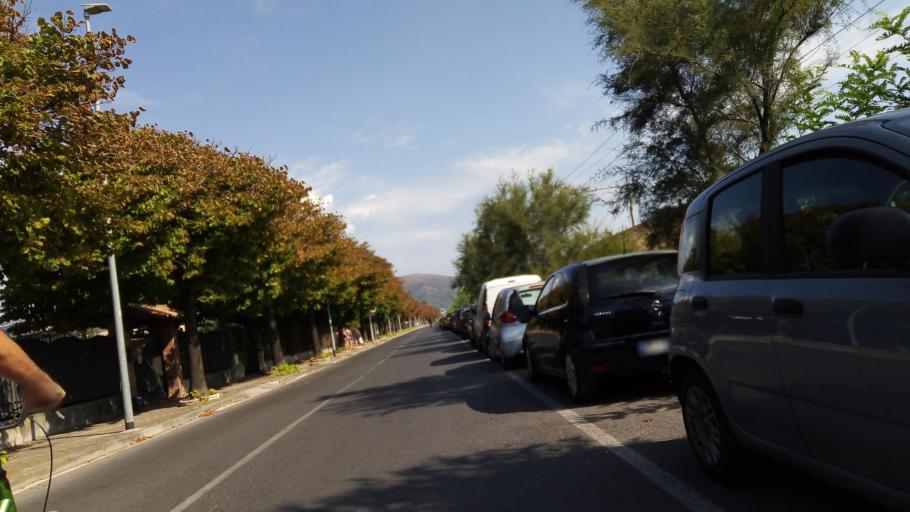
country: IT
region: Liguria
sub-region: Provincia di Savona
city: Albenga
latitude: 44.0563
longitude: 8.2252
